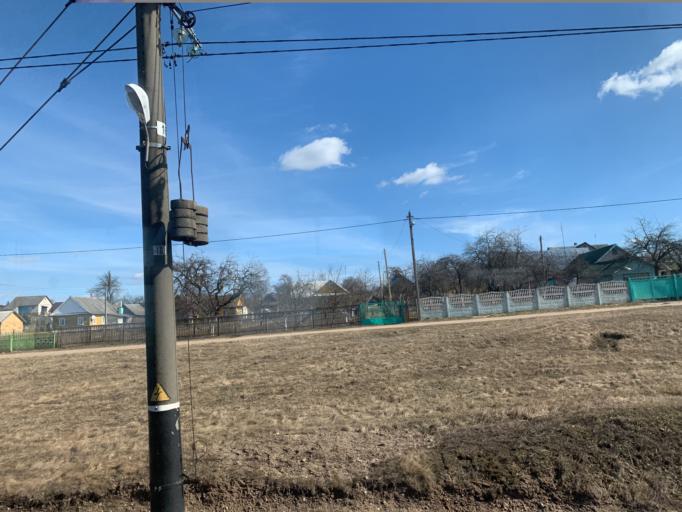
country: BY
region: Minsk
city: Haradzyeya
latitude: 53.3203
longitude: 26.5429
